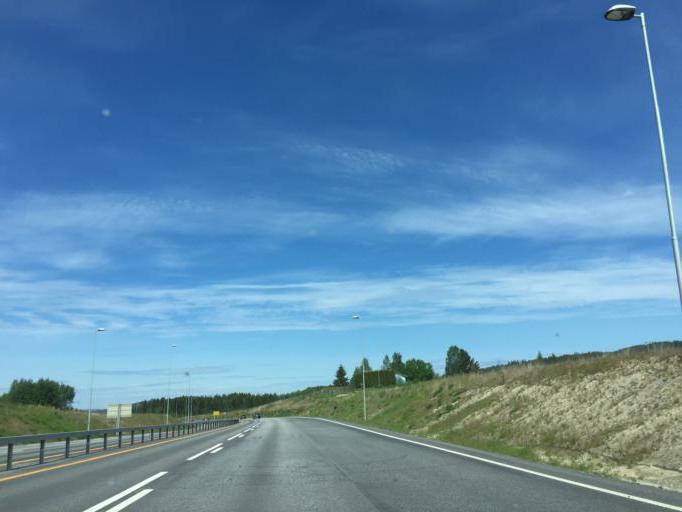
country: NO
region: Hedmark
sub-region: Kongsvinger
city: Spetalen
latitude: 60.2101
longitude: 11.8865
